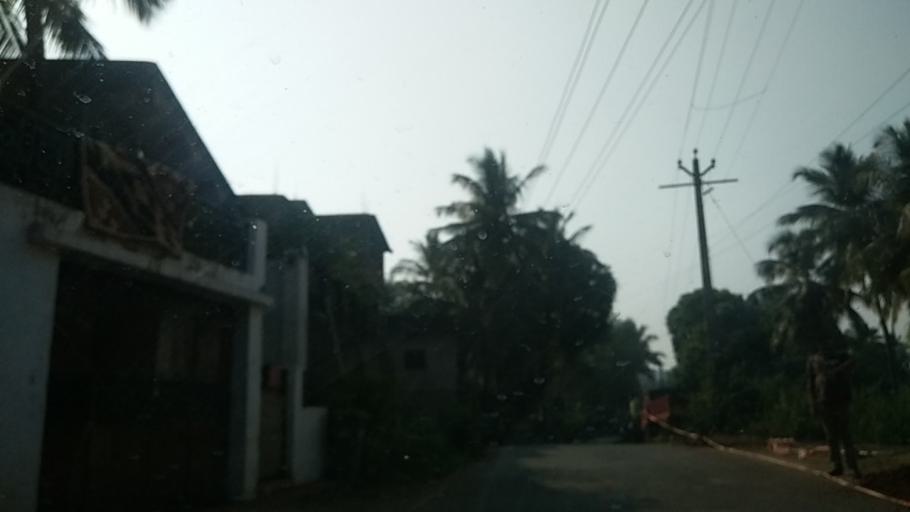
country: IN
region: Goa
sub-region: North Goa
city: Pernem
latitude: 15.7266
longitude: 73.7796
